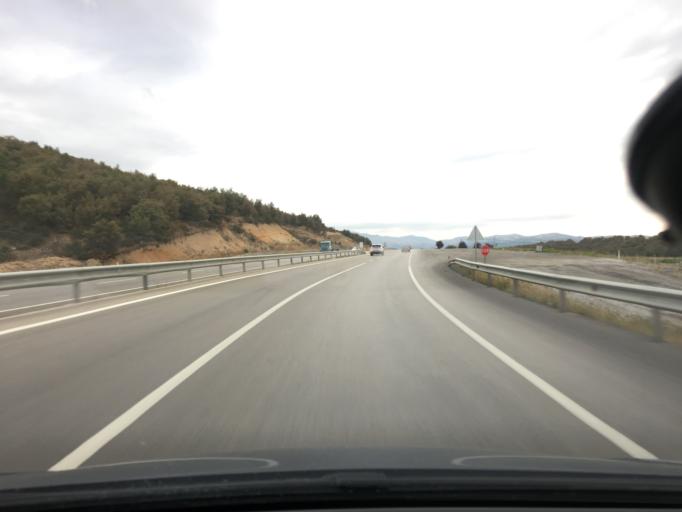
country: TR
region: Afyonkarahisar
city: Sincanli
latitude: 38.6750
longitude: 30.3246
